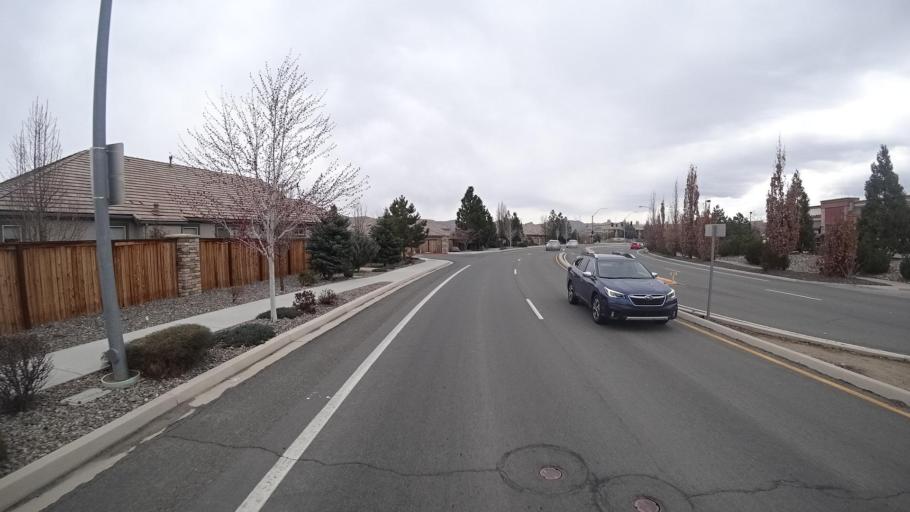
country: US
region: Nevada
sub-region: Washoe County
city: Sun Valley
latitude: 39.5831
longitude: -119.7373
